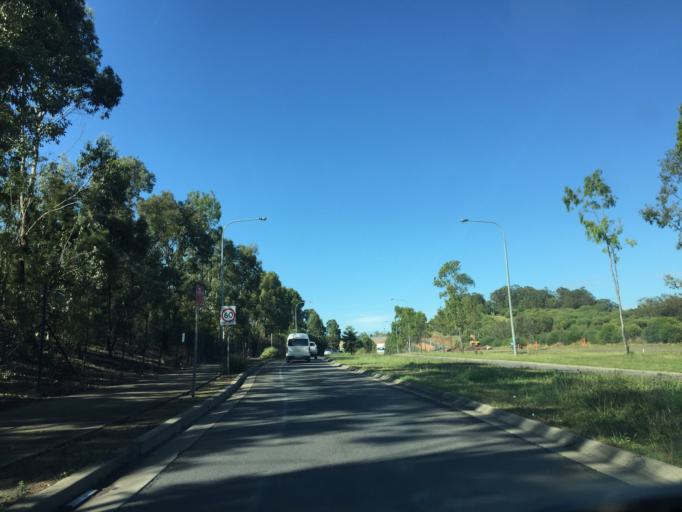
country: AU
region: New South Wales
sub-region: Holroyd
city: Girraween
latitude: -33.8162
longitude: 150.9208
